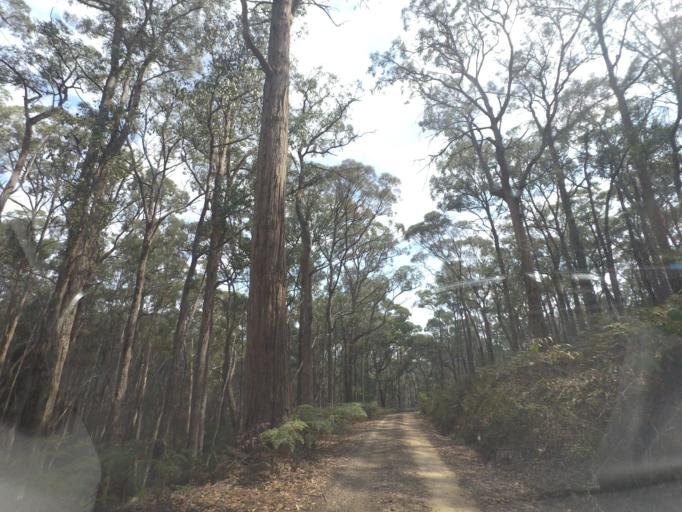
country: AU
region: Victoria
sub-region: Moorabool
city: Bacchus Marsh
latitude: -37.4640
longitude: 144.3699
